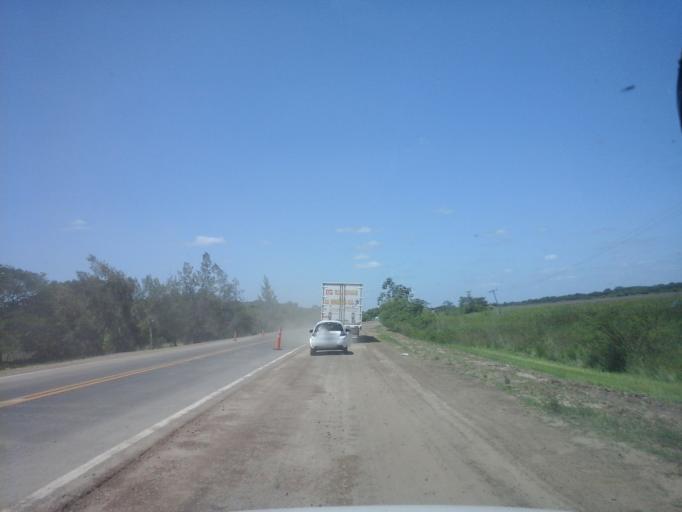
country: AR
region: Corrientes
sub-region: Departamento de Itati
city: Itati
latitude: -27.3465
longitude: -58.2305
